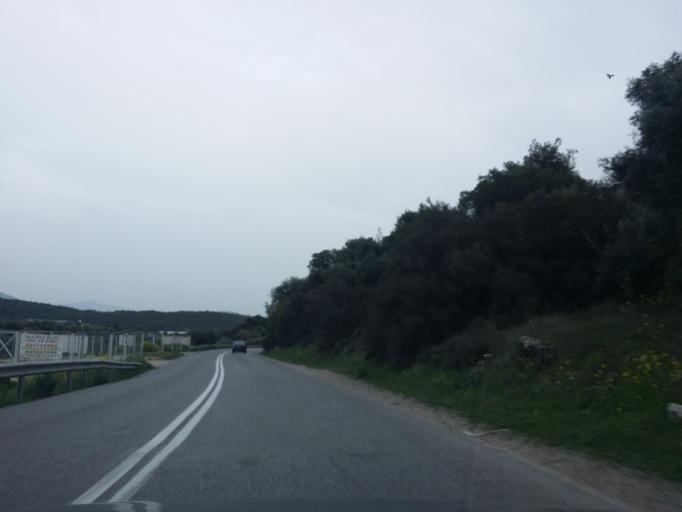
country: GR
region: Attica
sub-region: Nomarchia Dytikis Attikis
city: Mandra
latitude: 38.0854
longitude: 23.4849
